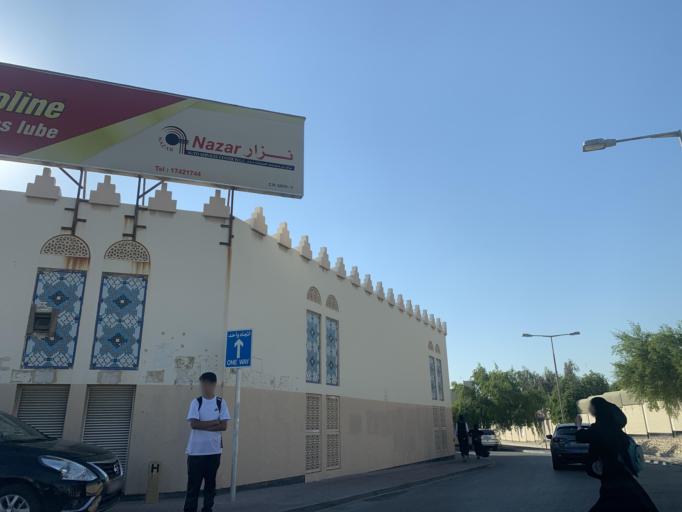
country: BH
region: Central Governorate
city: Madinat Hamad
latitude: 26.1073
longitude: 50.5064
